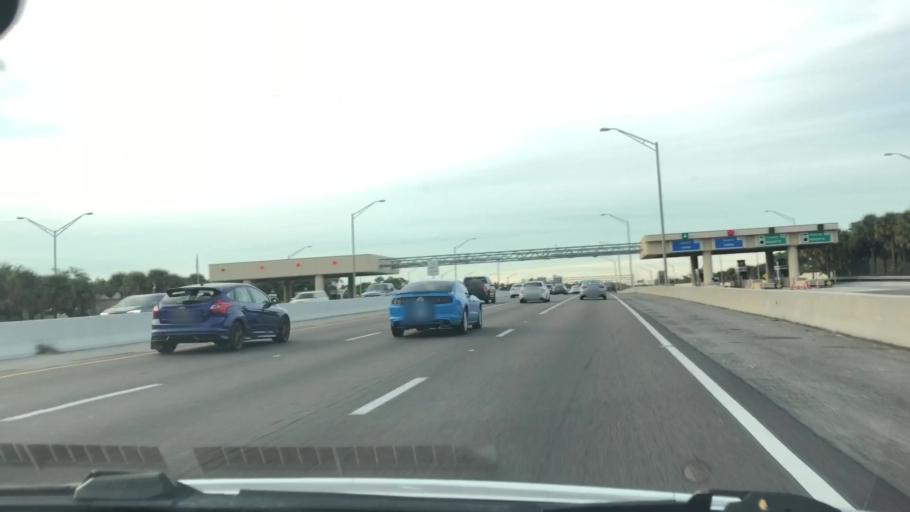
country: US
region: Florida
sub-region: Orange County
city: Azalea Park
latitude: 28.4868
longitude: -81.2417
